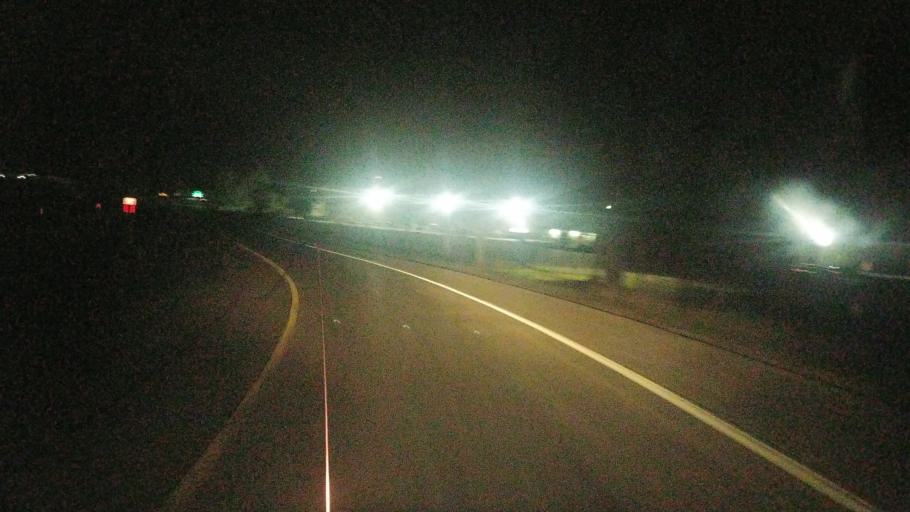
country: US
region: Michigan
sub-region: Washtenaw County
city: Milan
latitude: 42.0794
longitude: -83.6684
